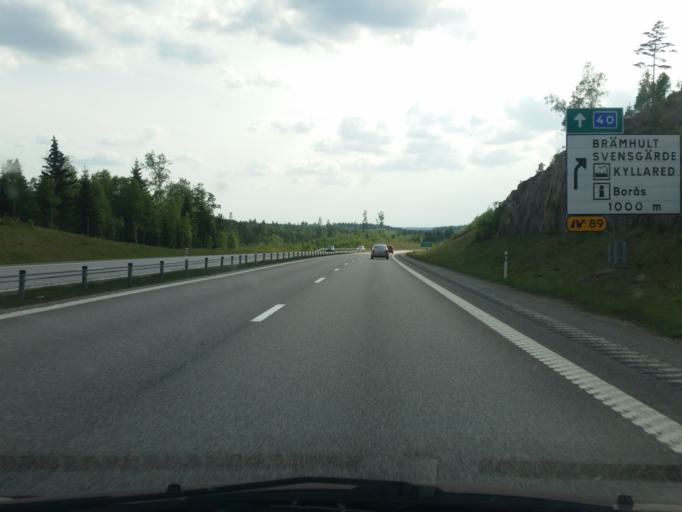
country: SE
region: Vaestra Goetaland
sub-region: Boras Kommun
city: Ganghester
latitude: 57.7337
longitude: 13.0366
